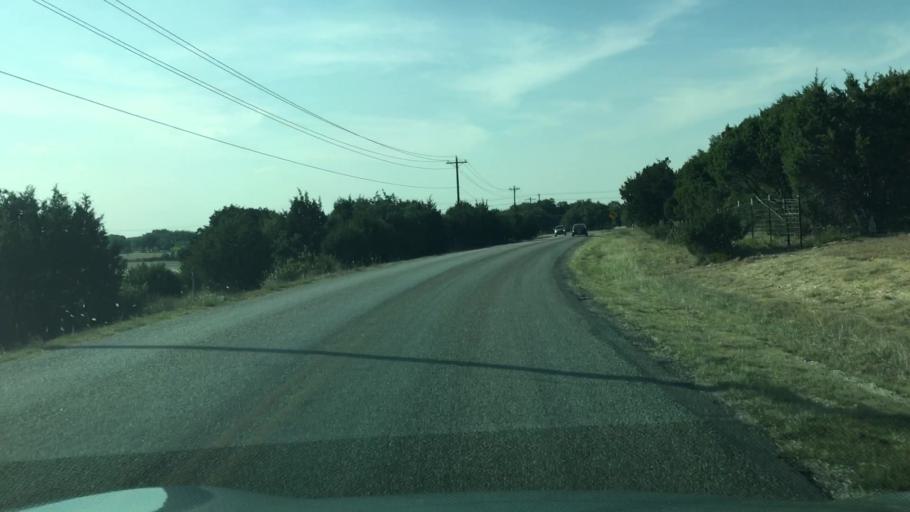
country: US
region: Texas
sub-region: Hays County
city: Dripping Springs
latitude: 30.1513
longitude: -97.9936
